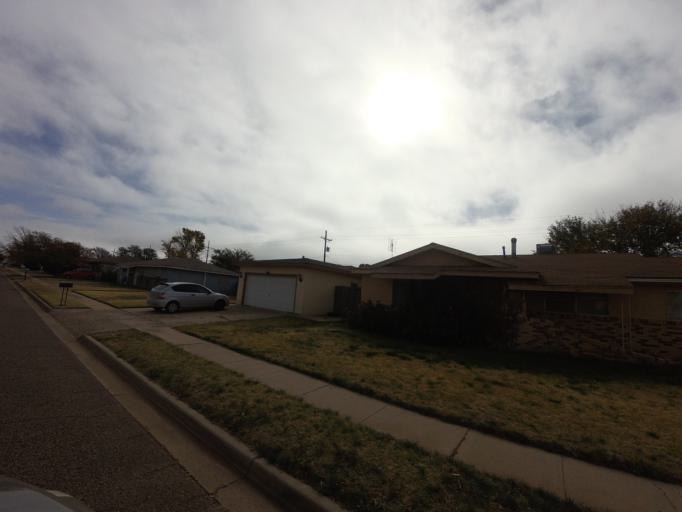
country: US
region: New Mexico
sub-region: Curry County
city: Clovis
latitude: 34.4270
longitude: -103.2220
